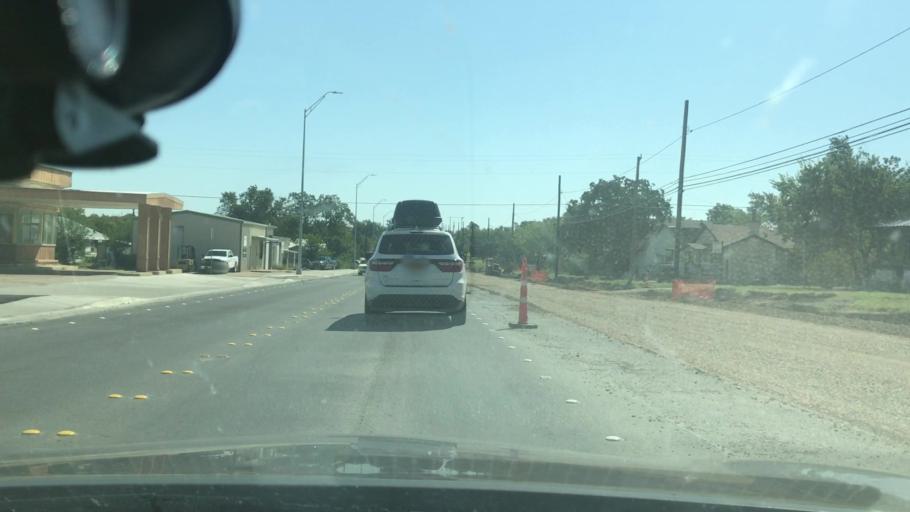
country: US
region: Texas
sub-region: Stephens County
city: Breckenridge
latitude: 32.7555
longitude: -98.8908
